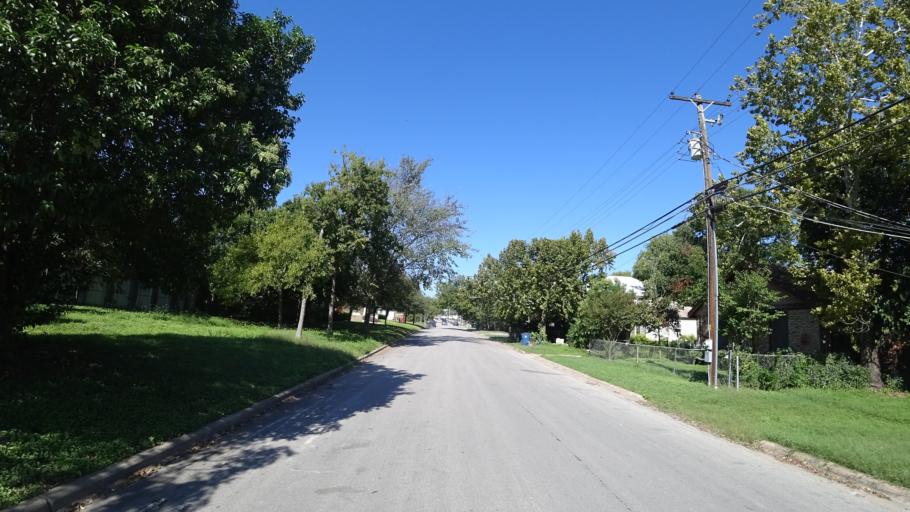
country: US
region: Texas
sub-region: Travis County
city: Austin
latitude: 30.3087
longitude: -97.7060
